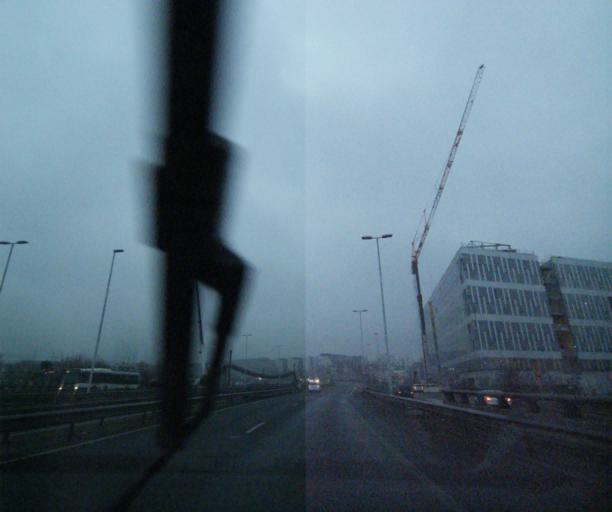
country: FR
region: Ile-de-France
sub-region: Departement des Hauts-de-Seine
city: Nanterre
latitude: 48.9033
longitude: 2.2191
